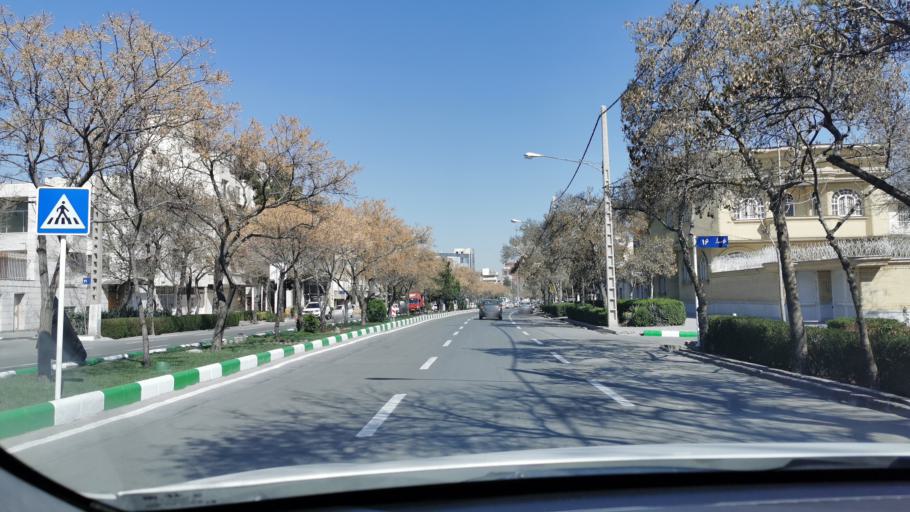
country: IR
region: Razavi Khorasan
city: Mashhad
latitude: 36.2905
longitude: 59.5723
